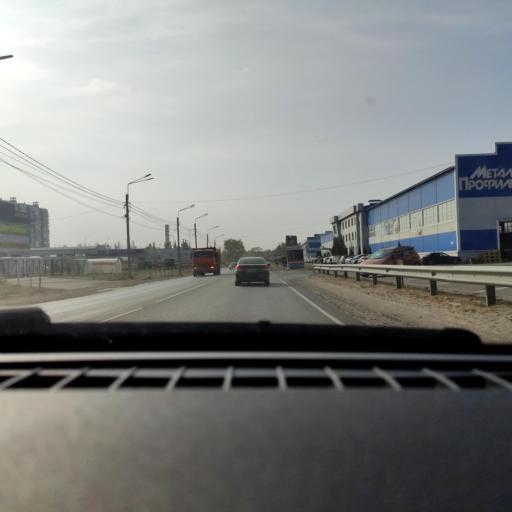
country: RU
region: Voronezj
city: Maslovka
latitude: 51.6384
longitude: 39.2924
